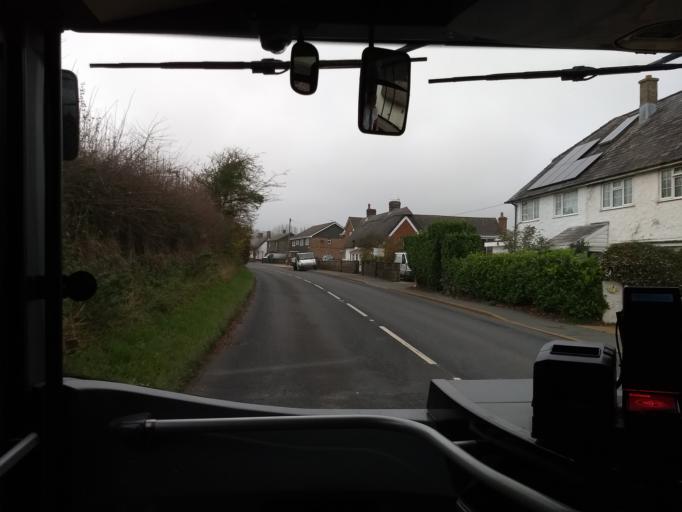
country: GB
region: England
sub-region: Isle of Wight
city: Newchurch
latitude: 50.6744
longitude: -1.2394
